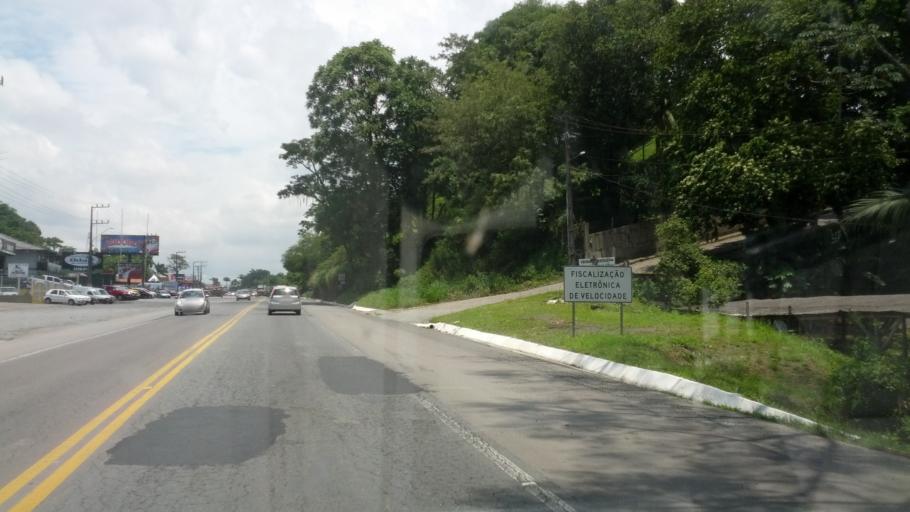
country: BR
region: Santa Catarina
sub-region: Blumenau
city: Blumenau
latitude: -26.8764
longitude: -49.1228
